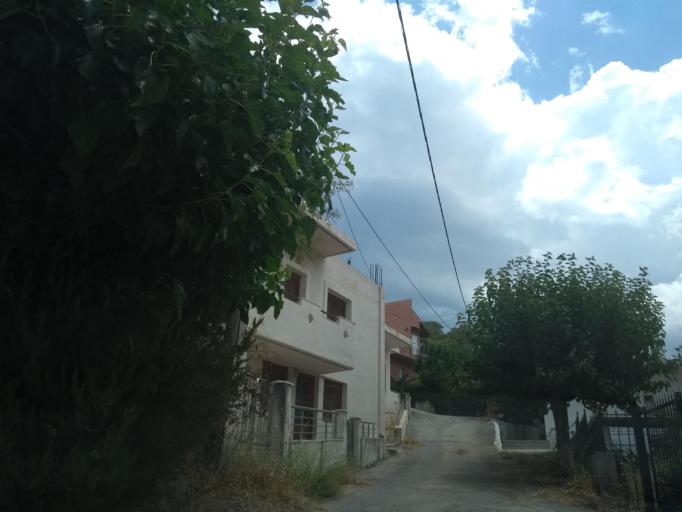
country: GR
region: Crete
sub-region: Nomos Chanias
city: Georgioupolis
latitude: 35.3791
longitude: 24.2459
